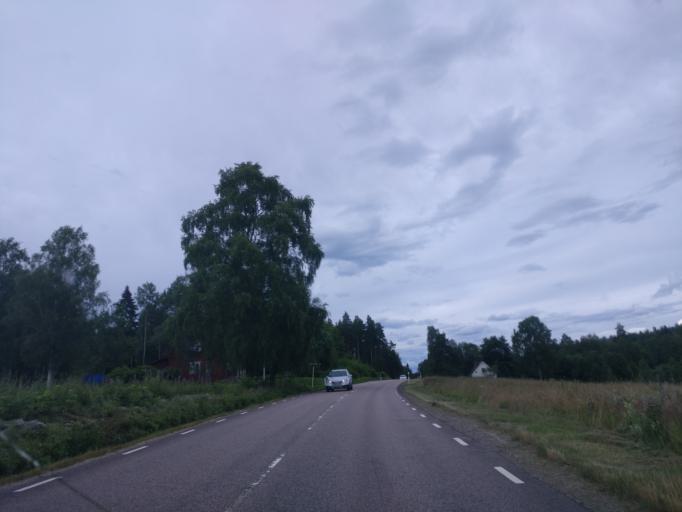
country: SE
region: Vaermland
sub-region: Hagfors Kommun
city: Ekshaerad
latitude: 60.1621
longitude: 13.4746
